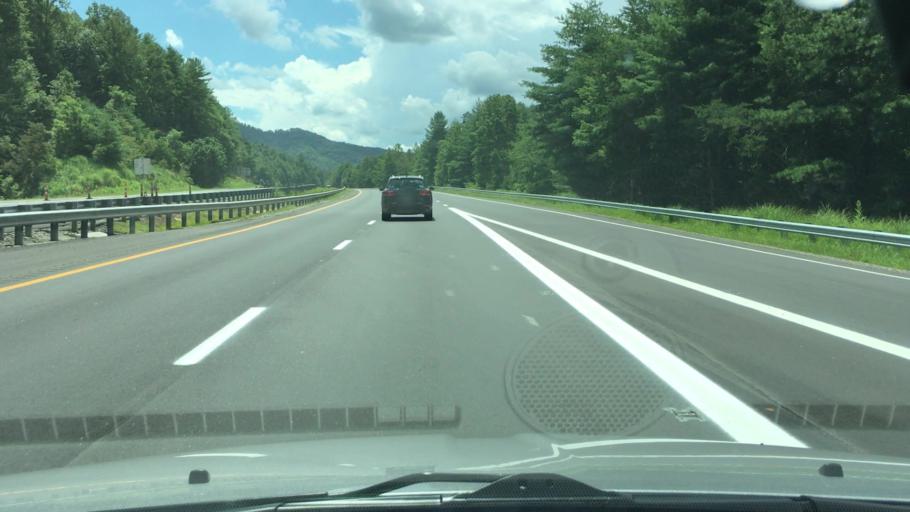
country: US
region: North Carolina
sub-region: Madison County
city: Mars Hill
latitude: 35.7812
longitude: -82.5401
